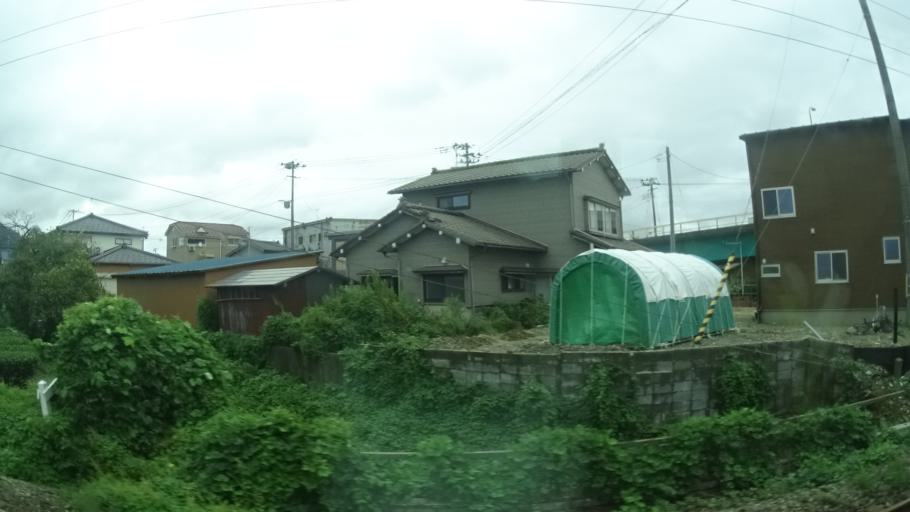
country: JP
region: Niigata
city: Murakami
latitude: 38.2239
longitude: 139.4635
